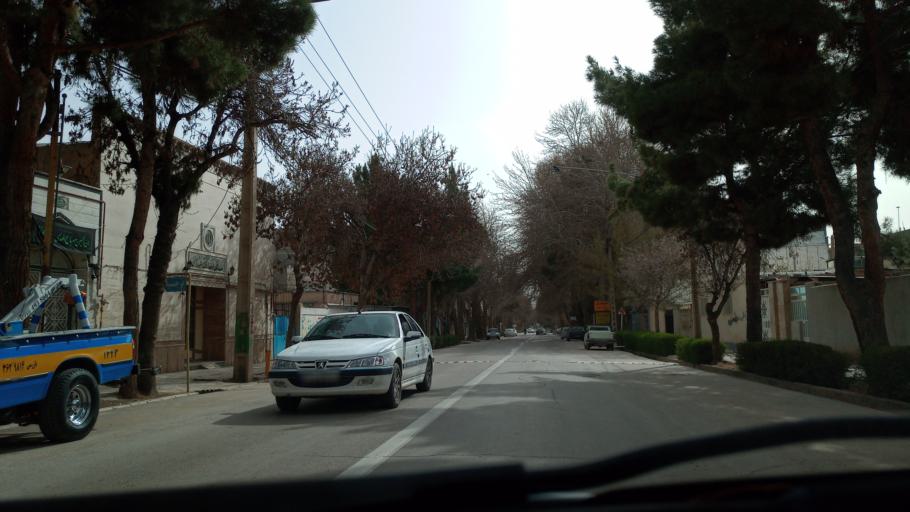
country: IR
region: Khorasan-e Shomali
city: Esfarayen
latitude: 37.0811
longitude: 57.5145
